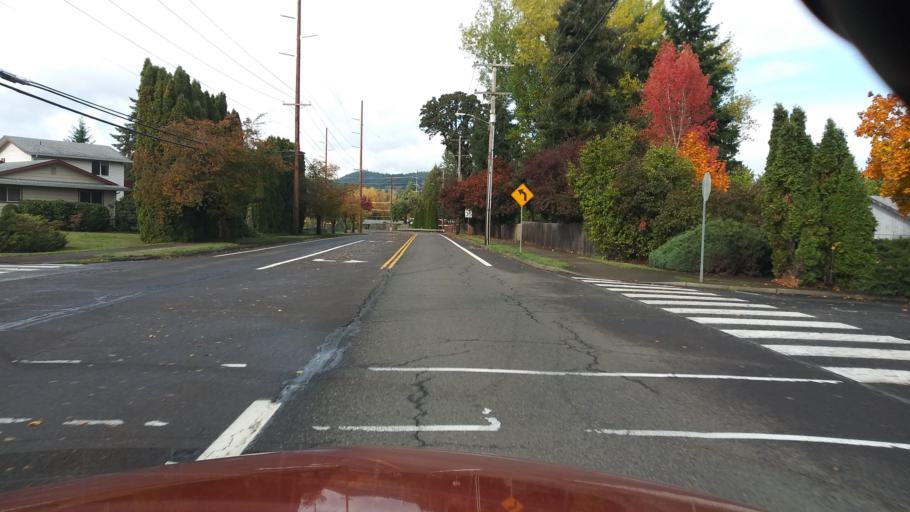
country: US
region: Oregon
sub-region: Washington County
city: Forest Grove
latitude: 45.5280
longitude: -123.1218
